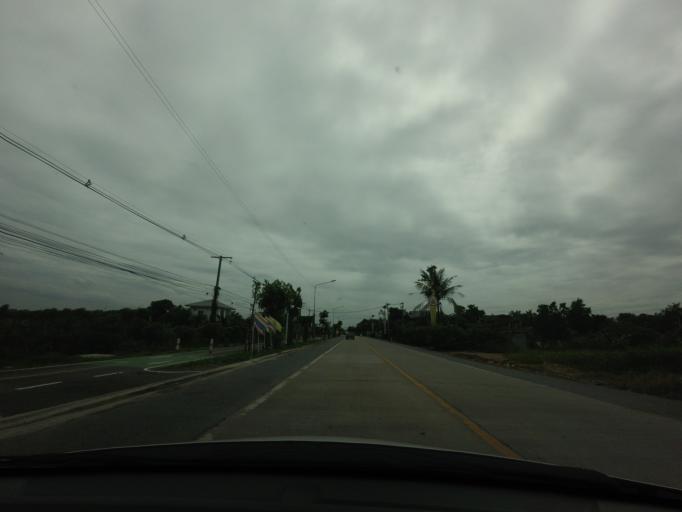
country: TH
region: Pathum Thani
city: Lam Luk Ka
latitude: 13.9296
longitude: 100.7296
